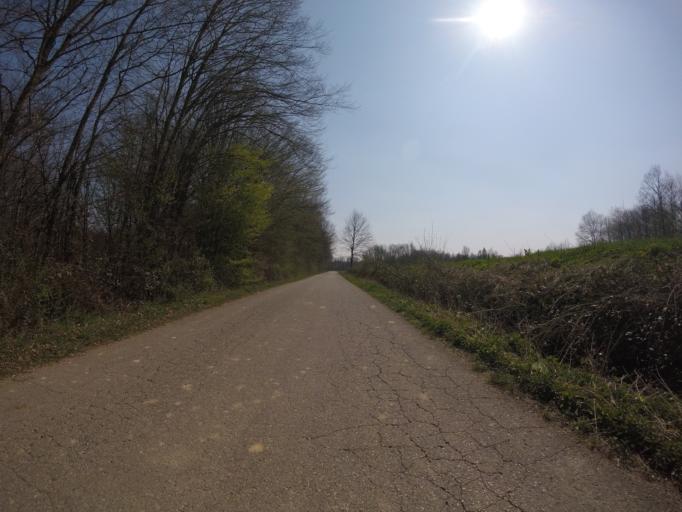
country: HR
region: Grad Zagreb
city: Strmec
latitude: 45.5671
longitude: 15.9207
